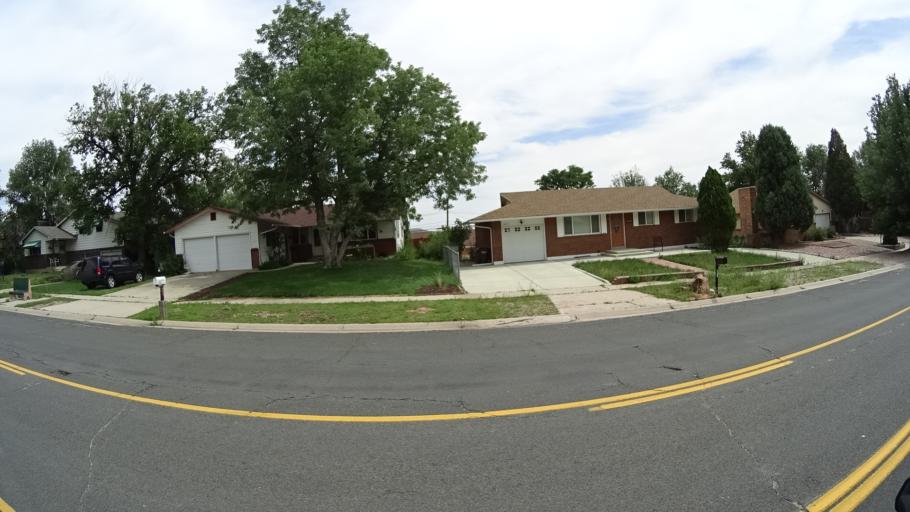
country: US
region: Colorado
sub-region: El Paso County
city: Colorado Springs
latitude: 38.8876
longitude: -104.8360
